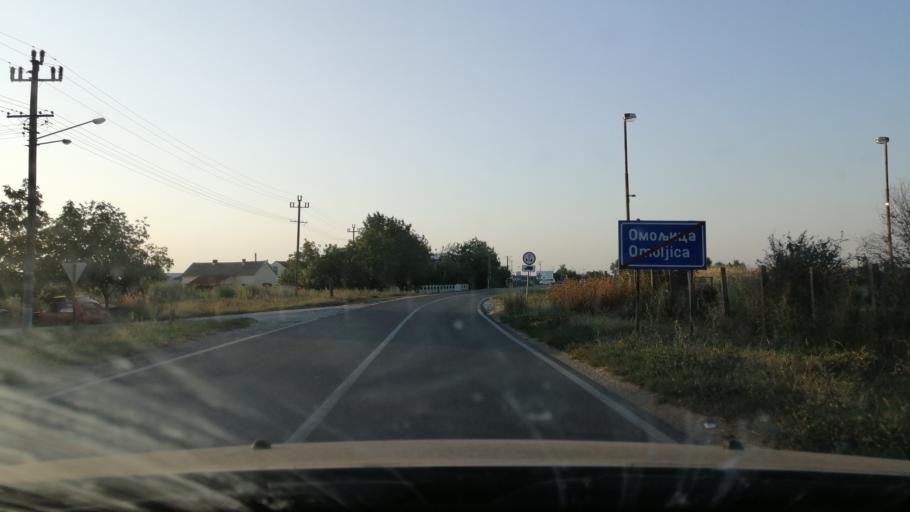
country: RS
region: Central Serbia
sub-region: Belgrade
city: Grocka
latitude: 44.7748
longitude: 20.7252
